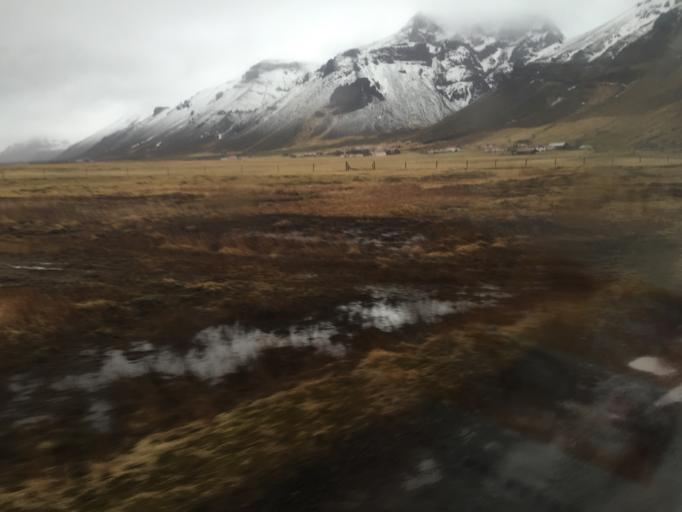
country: IS
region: East
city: Hoefn
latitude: 63.8986
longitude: -16.7040
